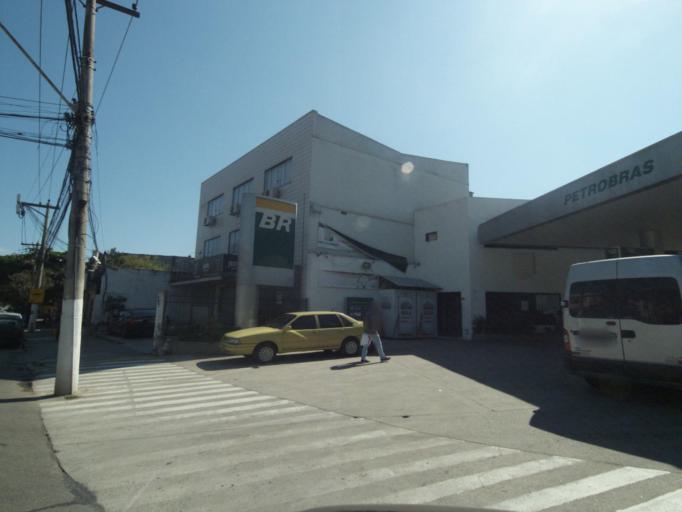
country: BR
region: Rio de Janeiro
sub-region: Niteroi
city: Niteroi
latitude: -22.8651
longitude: -43.1001
